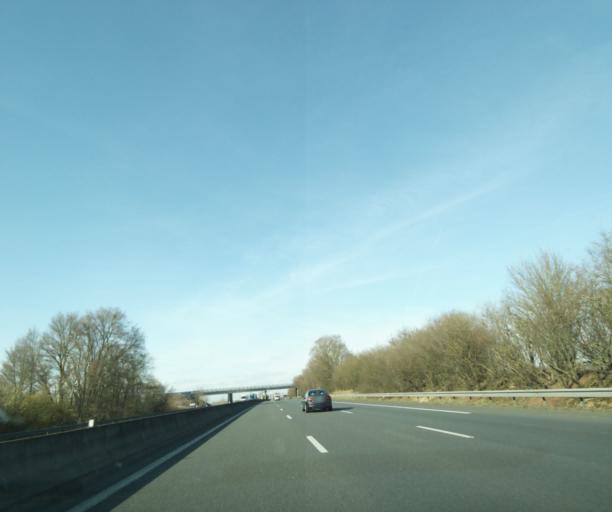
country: FR
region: Centre
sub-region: Departement du Loiret
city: Chevilly
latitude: 48.0386
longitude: 1.8402
